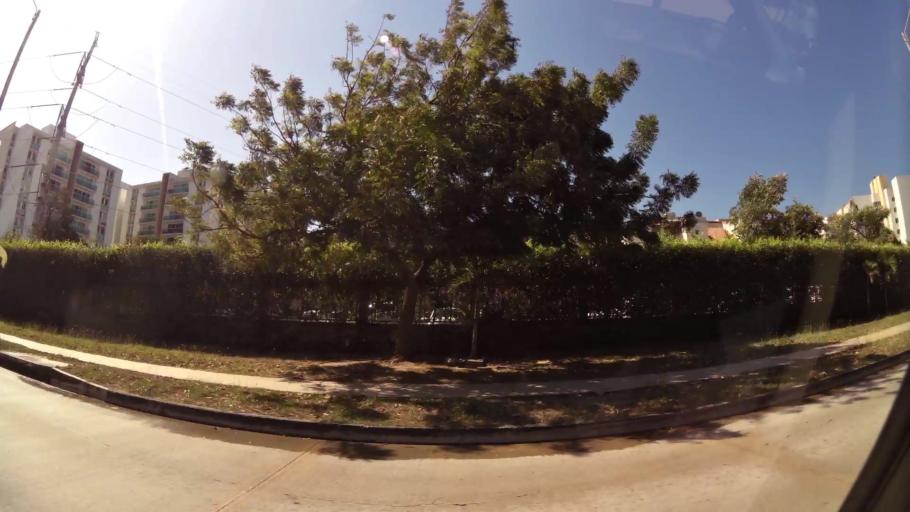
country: CO
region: Atlantico
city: Barranquilla
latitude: 11.0201
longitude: -74.8222
